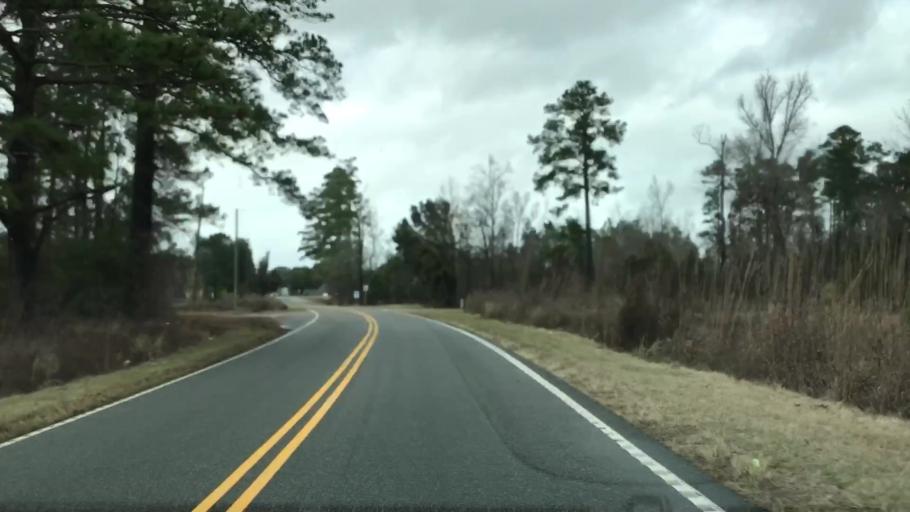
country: US
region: South Carolina
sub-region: Florence County
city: Johnsonville
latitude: 33.6608
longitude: -79.3048
